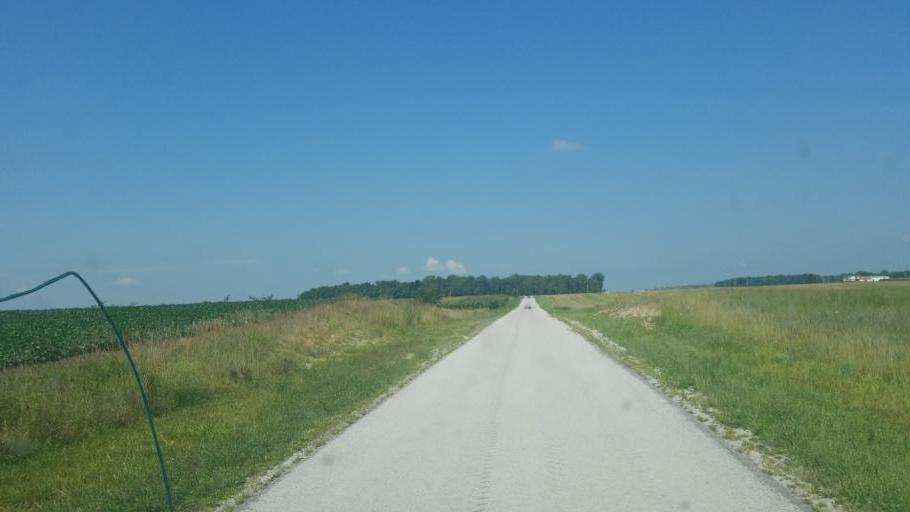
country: US
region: Ohio
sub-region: Hardin County
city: Kenton
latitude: 40.6752
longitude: -83.6443
